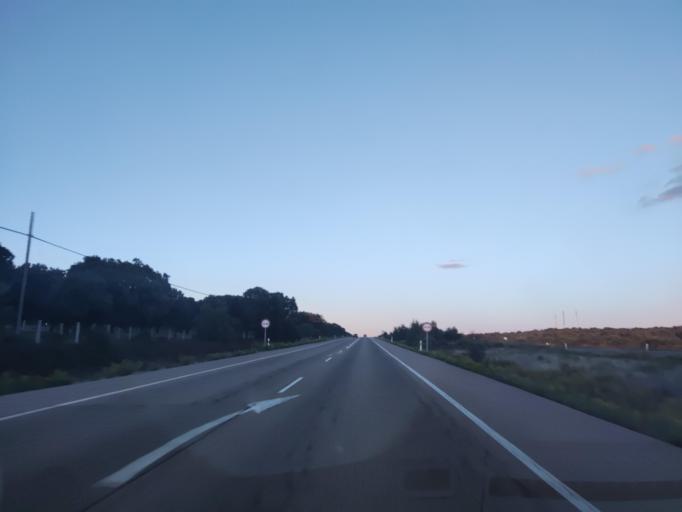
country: ES
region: Castille and Leon
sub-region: Provincia de Salamanca
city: San Munoz
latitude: 40.8141
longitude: -6.1352
